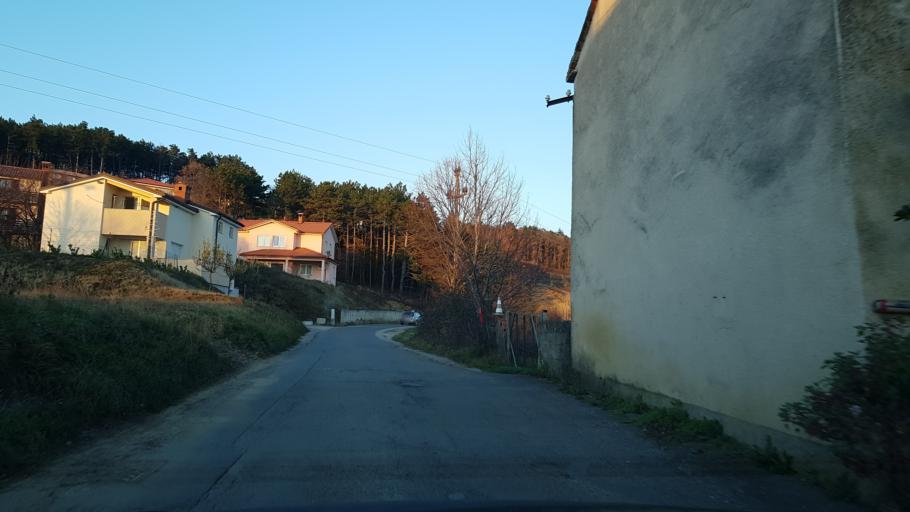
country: SI
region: Koper-Capodistria
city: Sv. Anton
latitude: 45.5000
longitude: 13.8562
